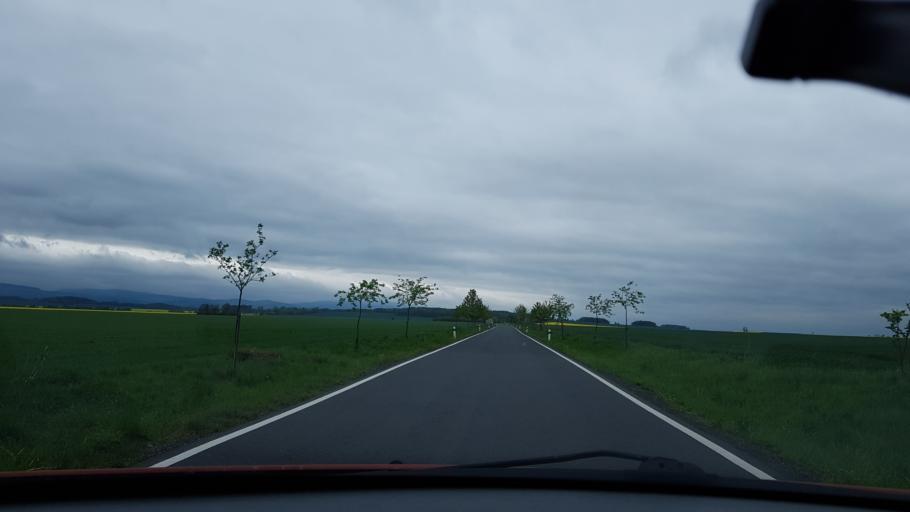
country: CZ
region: Olomoucky
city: Vidnava
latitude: 50.3773
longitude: 17.1723
